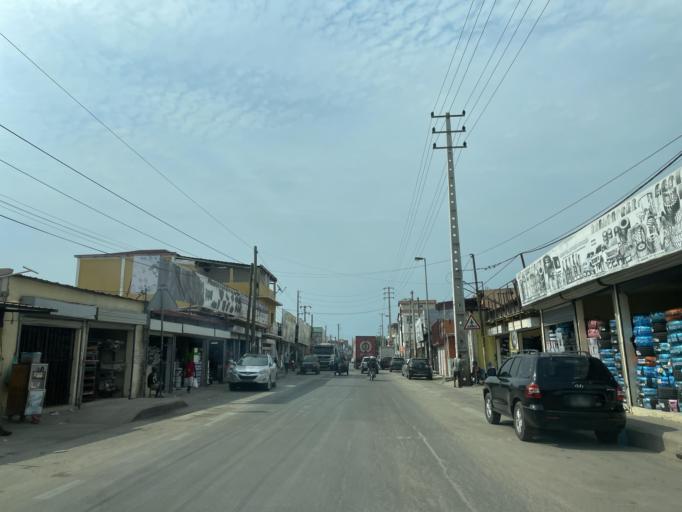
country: AO
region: Luanda
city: Luanda
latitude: -8.8999
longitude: 13.1868
